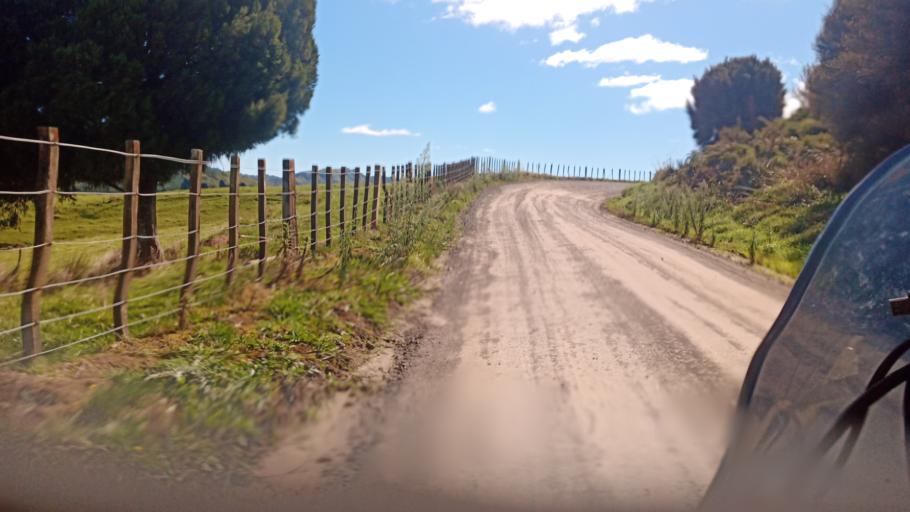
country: NZ
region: Bay of Plenty
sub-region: Opotiki District
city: Opotiki
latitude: -38.3037
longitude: 177.5615
